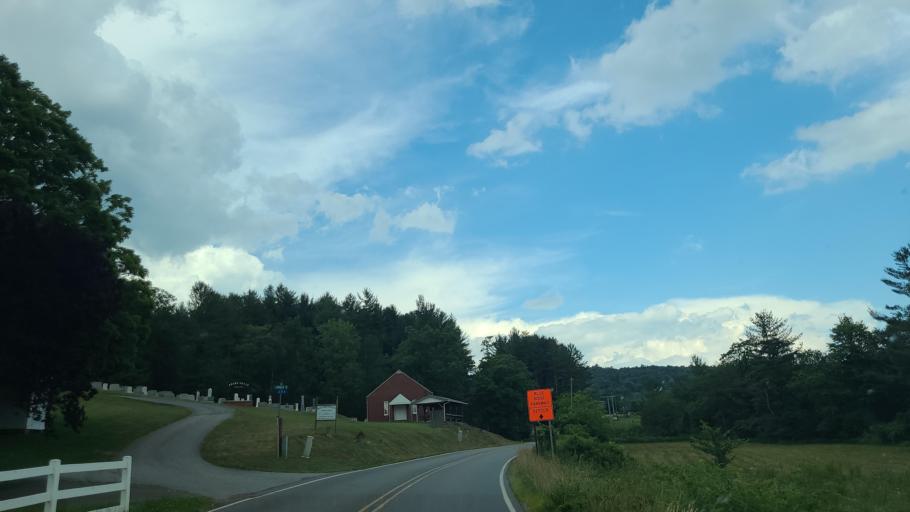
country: US
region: North Carolina
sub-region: Ashe County
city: Jefferson
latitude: 36.3898
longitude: -81.3583
